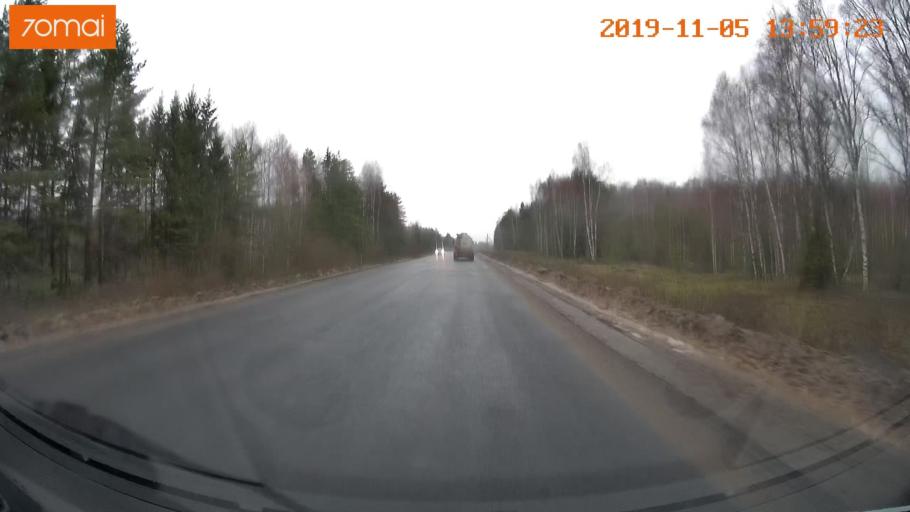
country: RU
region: Ivanovo
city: Kitovo
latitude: 57.0187
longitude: 41.2698
